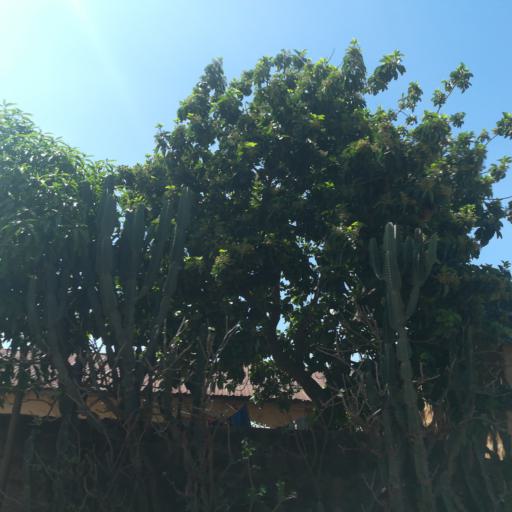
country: NG
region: Plateau
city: Bukuru
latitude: 9.7605
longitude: 8.8605
